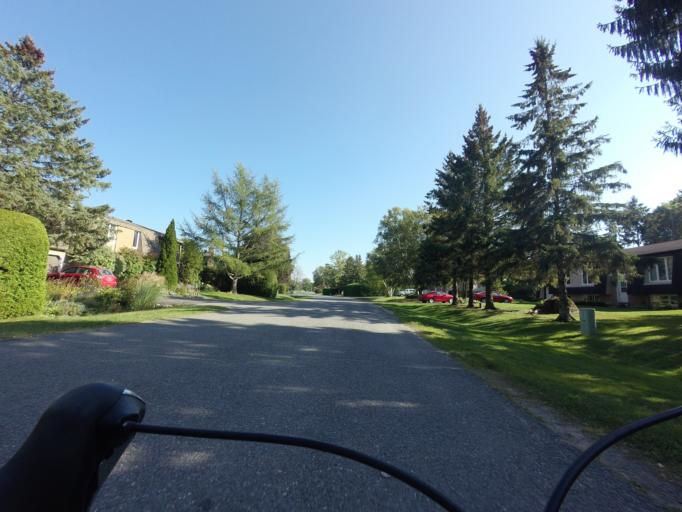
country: CA
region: Ontario
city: Bells Corners
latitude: 45.2326
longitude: -75.6846
